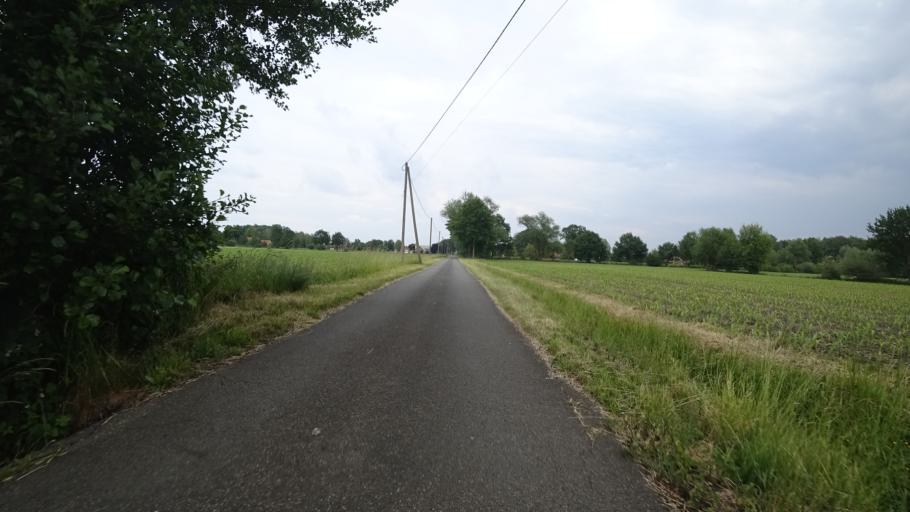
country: DE
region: North Rhine-Westphalia
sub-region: Regierungsbezirk Detmold
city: Guetersloh
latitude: 51.9504
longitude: 8.3366
